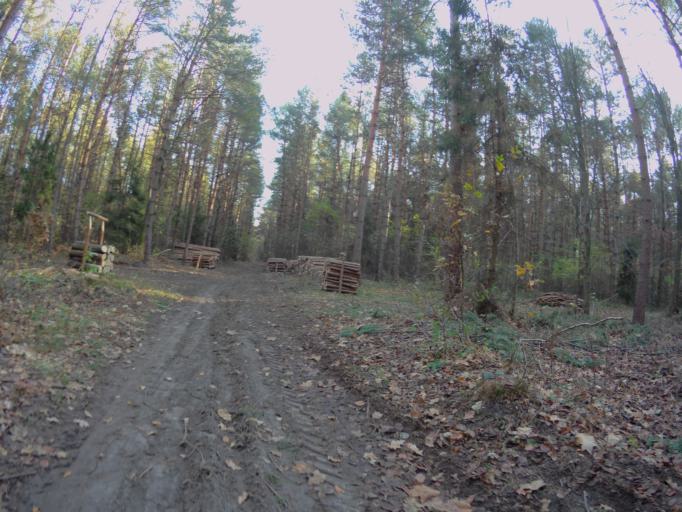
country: PL
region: Subcarpathian Voivodeship
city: Nowa Sarzyna
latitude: 50.3081
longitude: 22.3517
